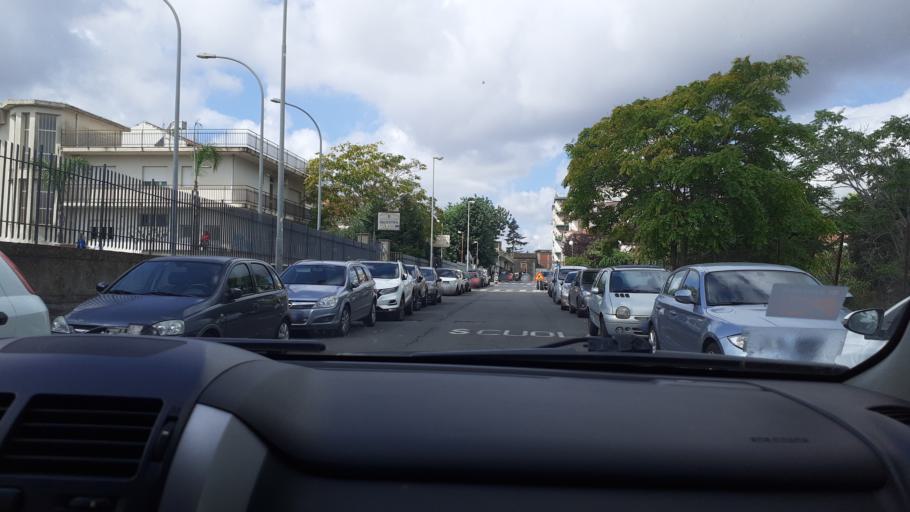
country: IT
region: Sicily
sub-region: Catania
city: San Giovanni la Punta
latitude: 37.5809
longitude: 15.0984
